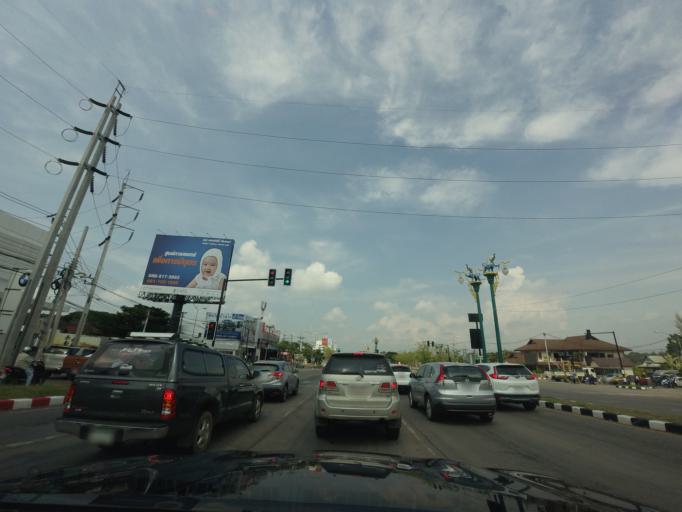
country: TH
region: Khon Kaen
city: Khon Kaen
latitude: 16.4408
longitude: 102.8196
